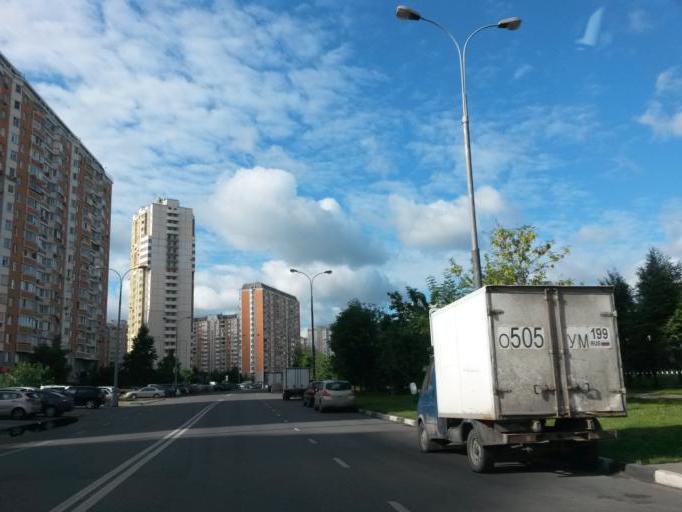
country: RU
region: Moscow
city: Brateyevo
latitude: 55.6616
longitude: 37.7727
